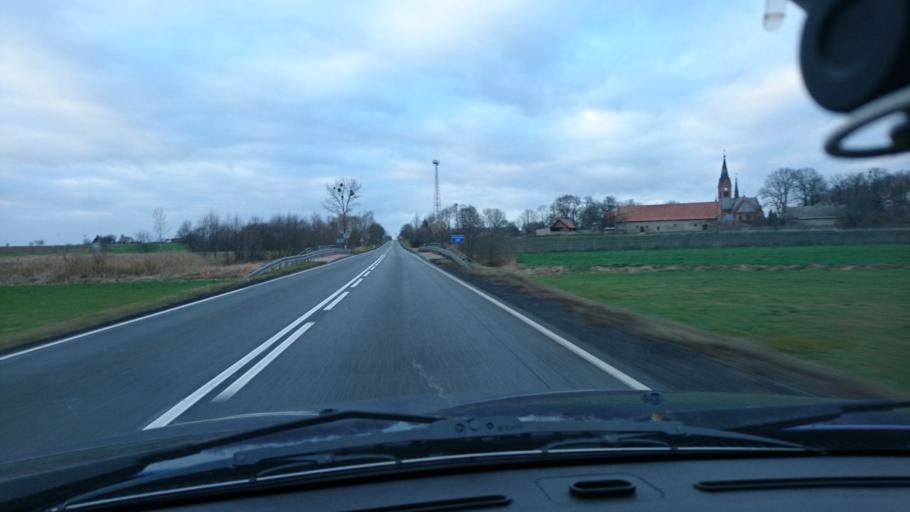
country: PL
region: Greater Poland Voivodeship
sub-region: Powiat kepinski
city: Opatow
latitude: 51.2097
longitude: 18.1458
